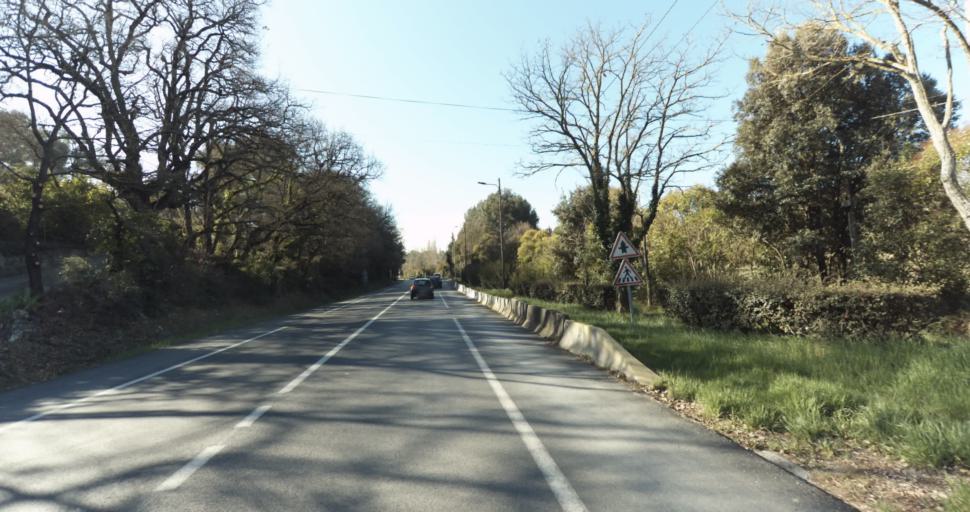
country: FR
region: Provence-Alpes-Cote d'Azur
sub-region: Departement des Bouches-du-Rhone
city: Aix-en-Provence
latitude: 43.5562
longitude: 5.4339
